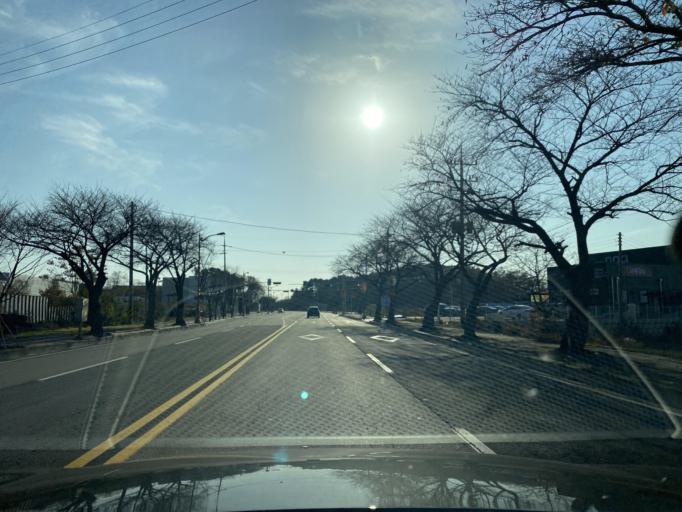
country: KR
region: Chungcheongnam-do
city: Yesan
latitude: 36.7191
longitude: 126.8456
